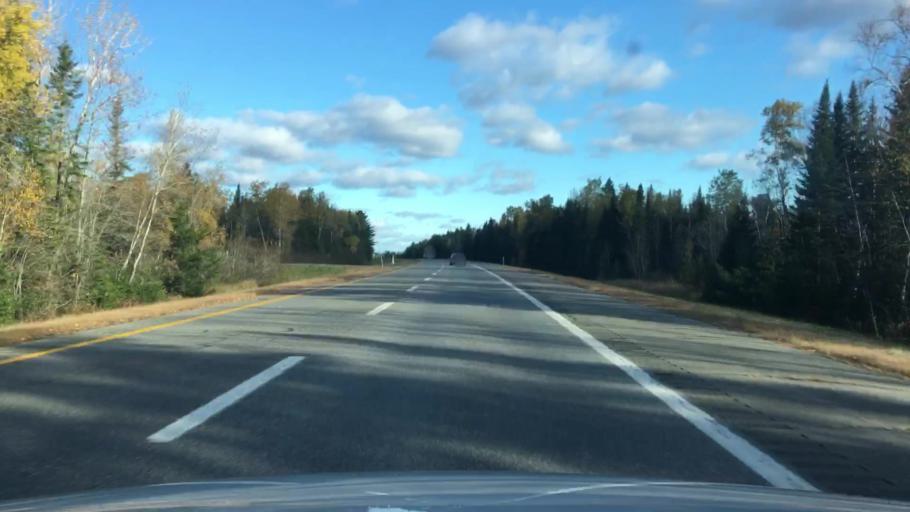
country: US
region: Maine
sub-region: Penobscot County
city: Greenbush
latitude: 45.1216
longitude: -68.6940
